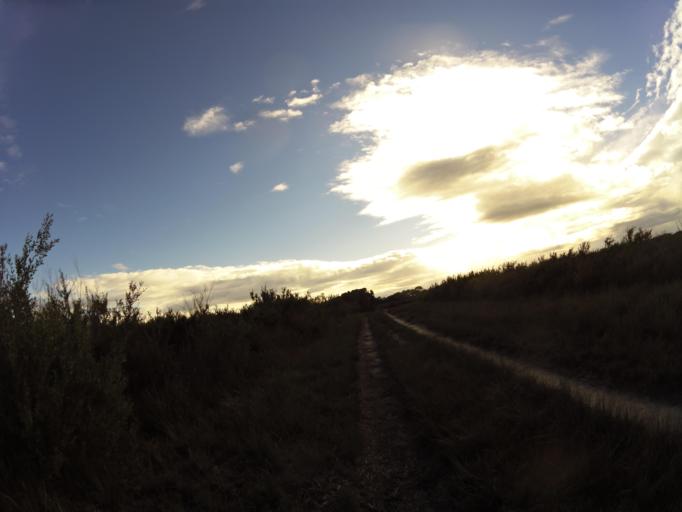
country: AU
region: Victoria
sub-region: Bass Coast
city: North Wonthaggi
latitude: -38.6409
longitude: 145.5668
